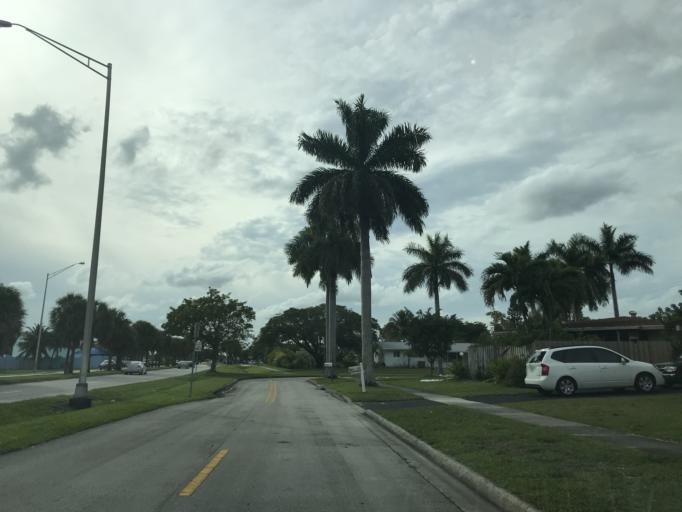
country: US
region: Florida
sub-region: Broward County
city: Margate
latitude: 26.2548
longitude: -80.2078
